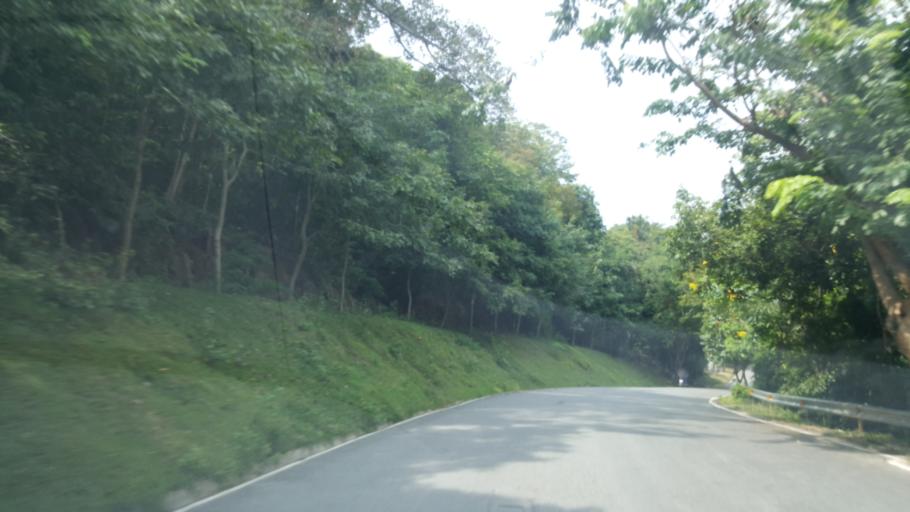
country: TH
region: Chon Buri
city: Ban Bueng
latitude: 13.2112
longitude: 101.0615
